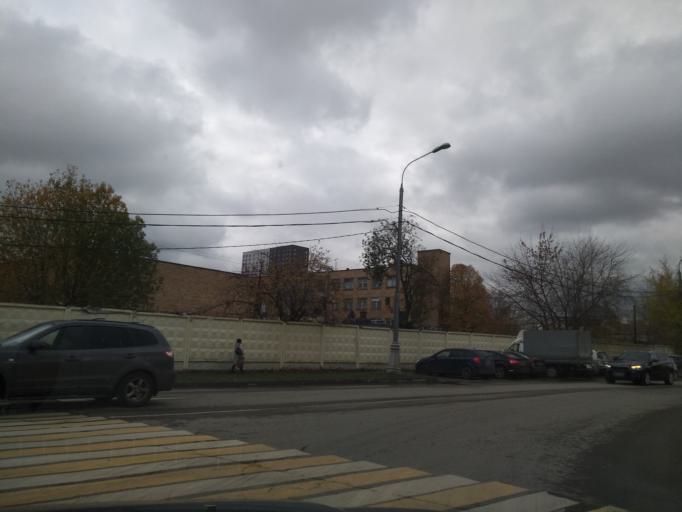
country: RU
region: Moscow
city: Kozeyevo
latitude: 55.8850
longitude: 37.6310
